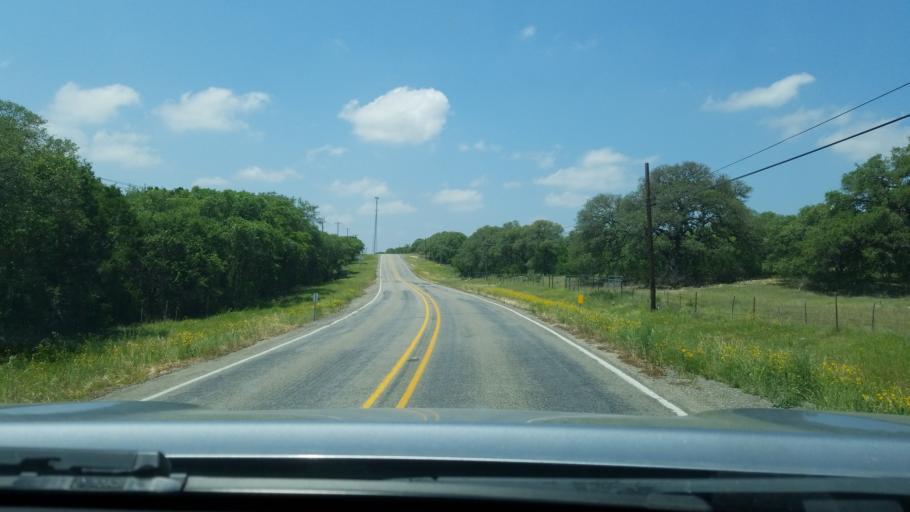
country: US
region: Texas
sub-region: Hays County
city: Woodcreek
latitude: 30.0434
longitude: -98.1931
